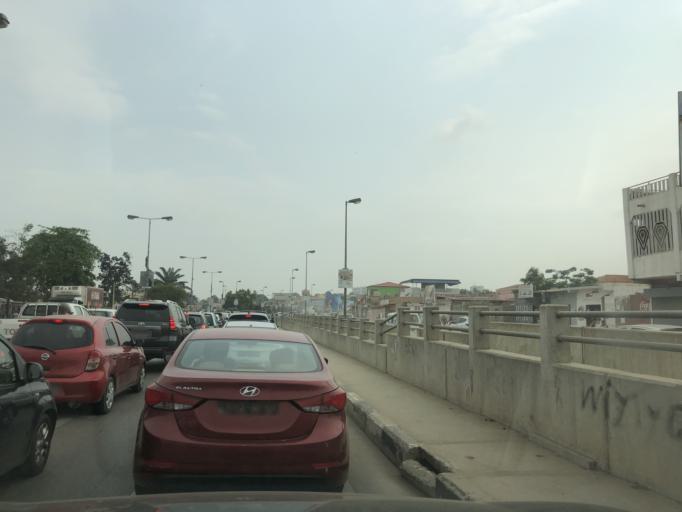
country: AO
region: Luanda
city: Luanda
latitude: -8.8497
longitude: 13.2105
